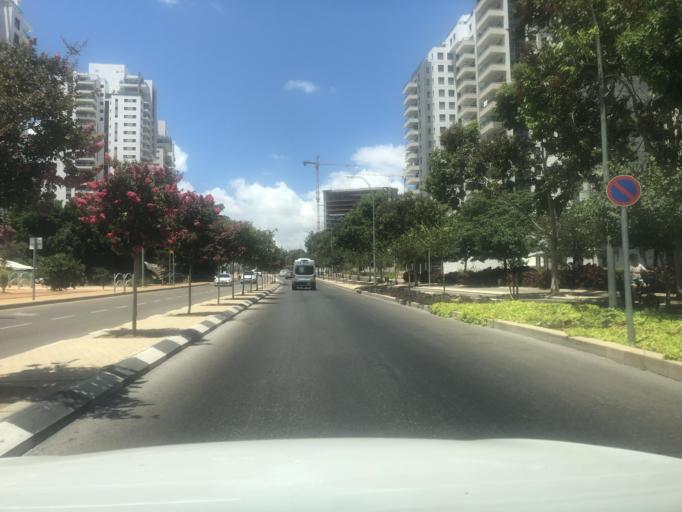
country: IL
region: Central District
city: Hod HaSharon
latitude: 32.1647
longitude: 34.9021
